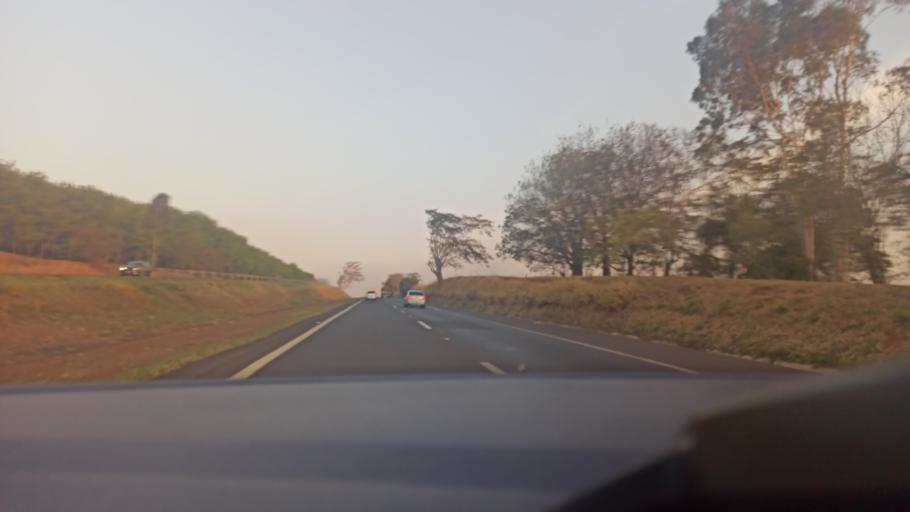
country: BR
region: Sao Paulo
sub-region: Taquaritinga
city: Taquaritinga
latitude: -21.4521
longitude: -48.6328
